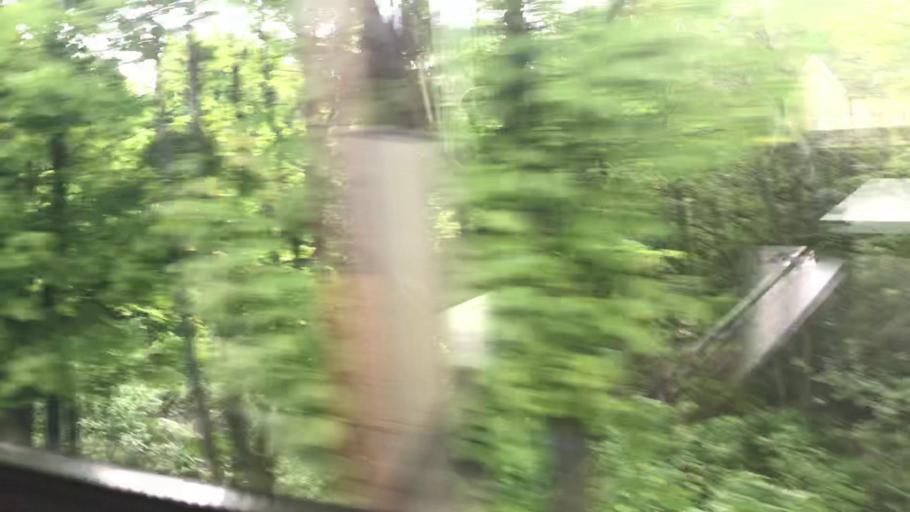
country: PL
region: Lower Silesian Voivodeship
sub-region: Powiat walbrzyski
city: Walbrzych
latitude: 50.7678
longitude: 16.2524
